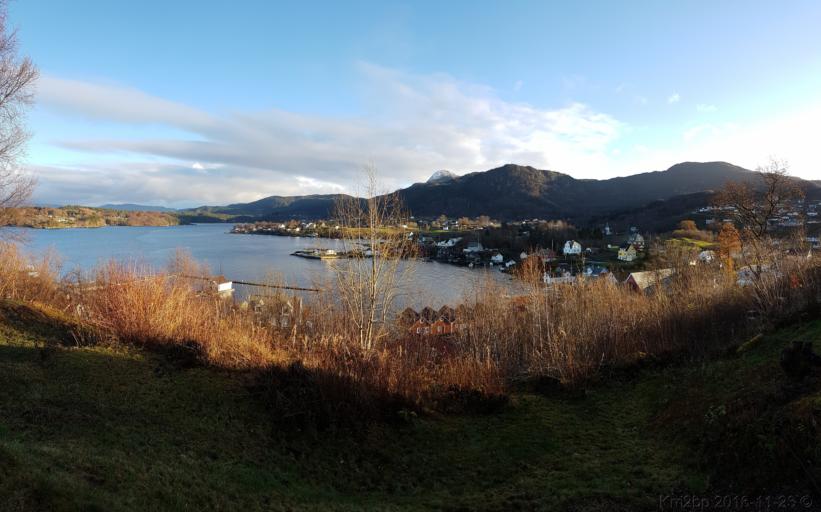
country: NO
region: Hordaland
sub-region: Tysnes
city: Uggdal
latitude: 60.0444
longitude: 5.5269
